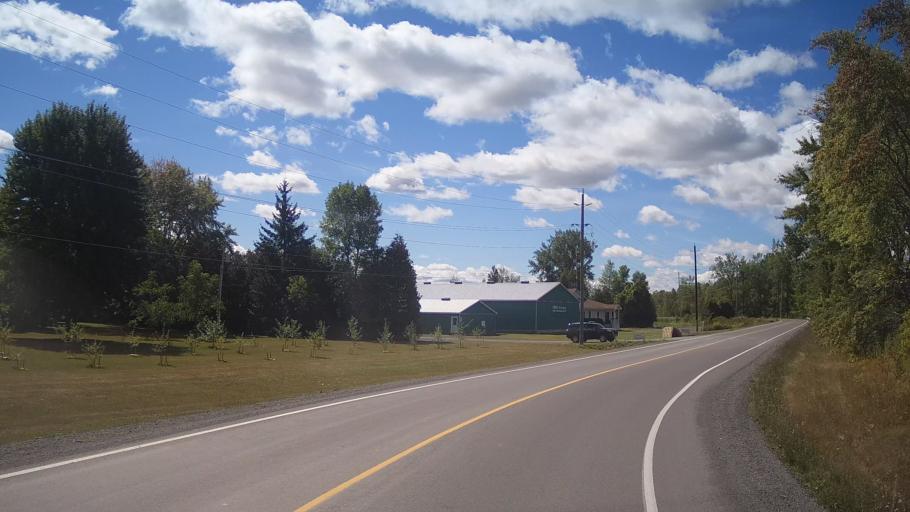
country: US
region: New York
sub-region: St. Lawrence County
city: Ogdensburg
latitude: 44.8402
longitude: -75.3182
